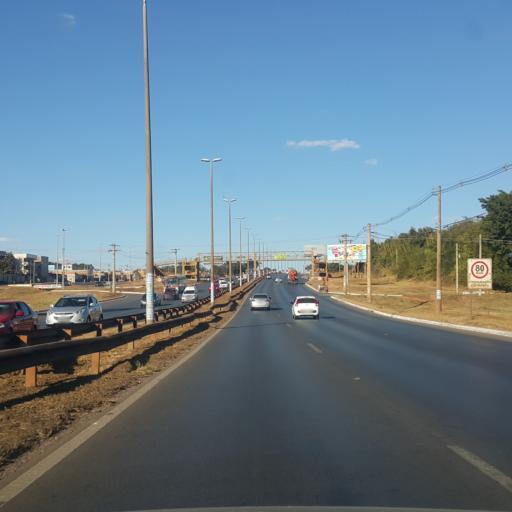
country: BR
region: Federal District
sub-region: Brasilia
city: Brasilia
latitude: -15.7863
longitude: -48.0029
